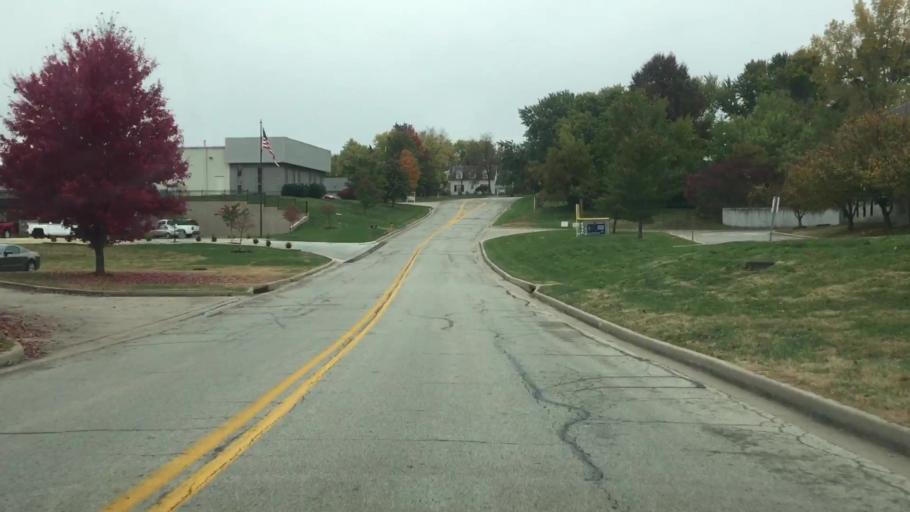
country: US
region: Kansas
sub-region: Wyandotte County
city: Edwardsville
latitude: 39.0016
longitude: -94.8246
